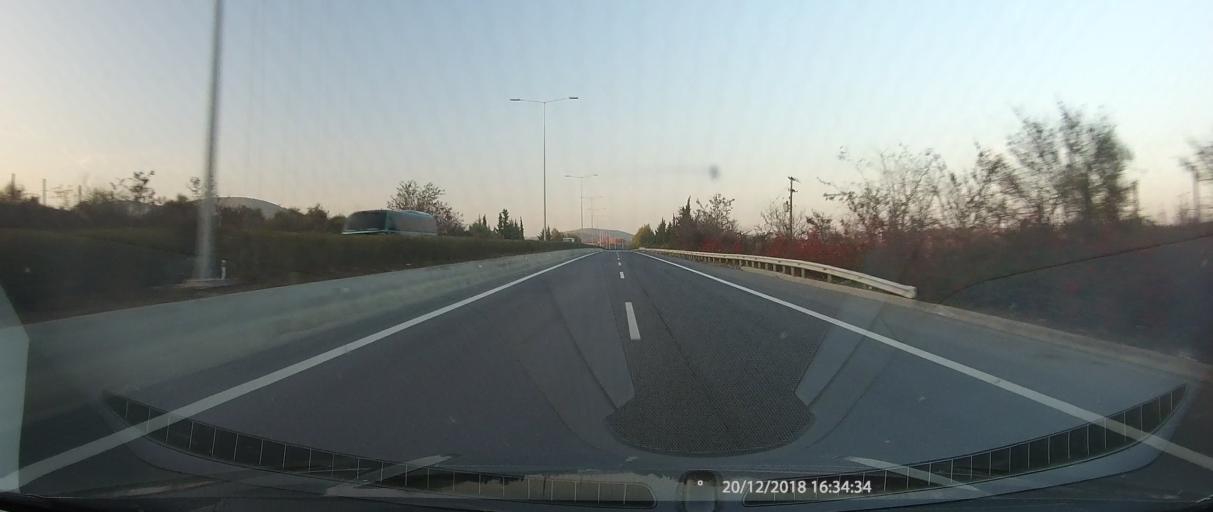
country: GR
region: Thessaly
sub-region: Nomos Magnisias
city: Nea Anchialos
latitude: 39.2854
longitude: 22.7449
